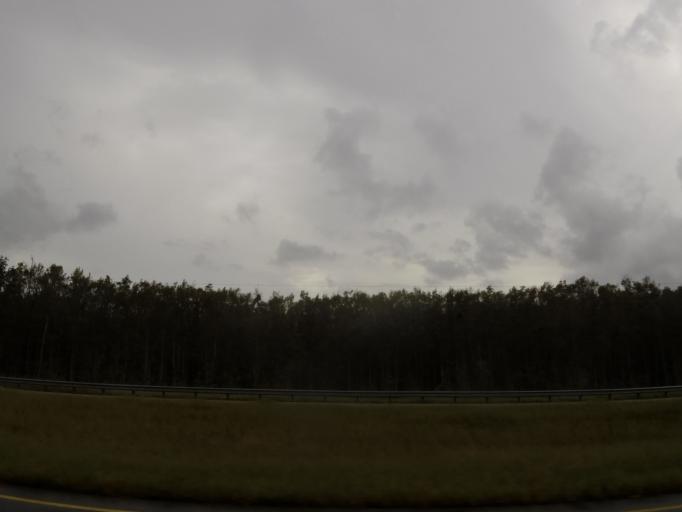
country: US
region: Georgia
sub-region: Wayne County
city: Jesup
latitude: 31.4657
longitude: -81.7151
